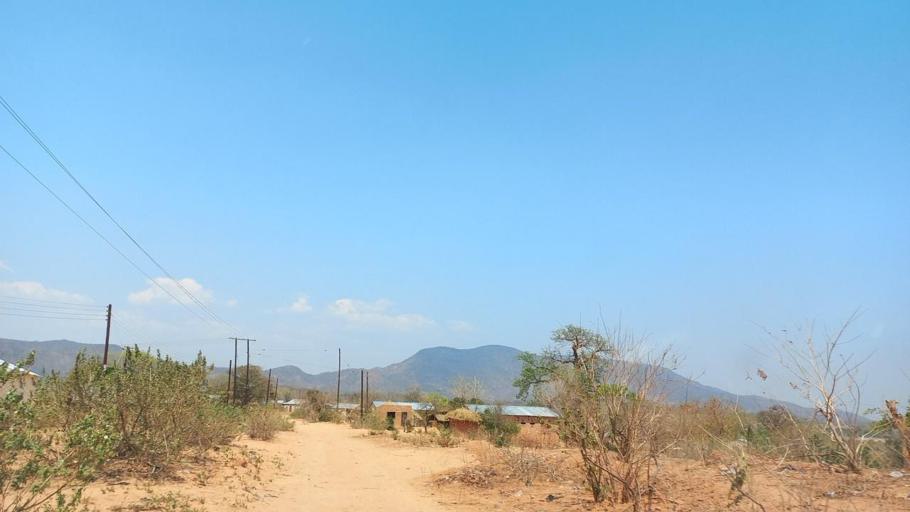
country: ZM
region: Lusaka
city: Luangwa
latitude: -15.5901
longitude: 30.3920
